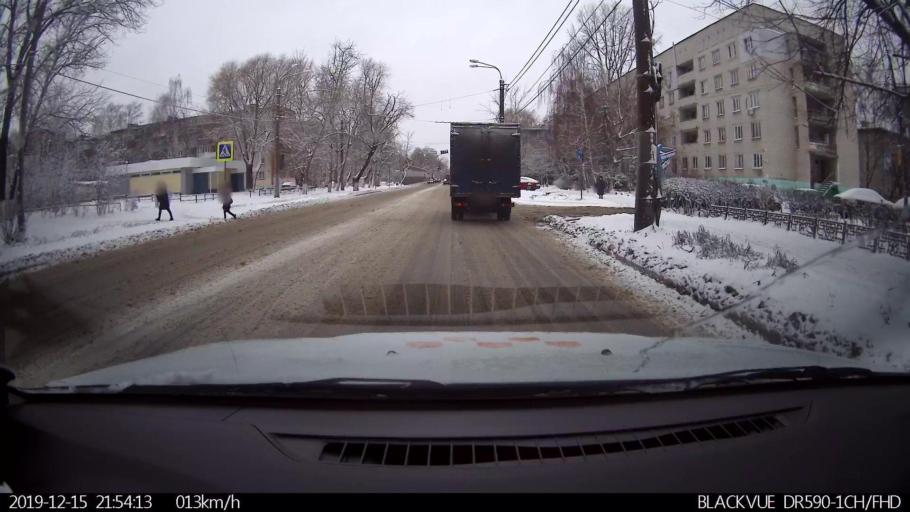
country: RU
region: Nizjnij Novgorod
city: Burevestnik
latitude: 56.2338
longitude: 43.8774
